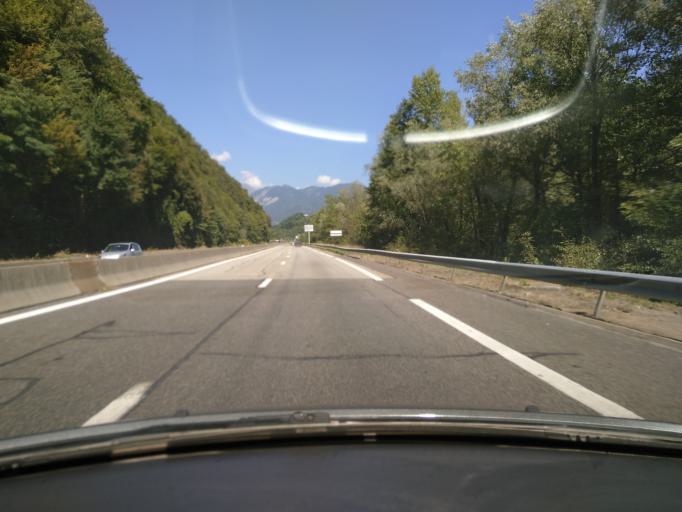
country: FR
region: Rhone-Alpes
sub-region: Departement de la Savoie
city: Albertville
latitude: 45.6948
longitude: 6.4028
